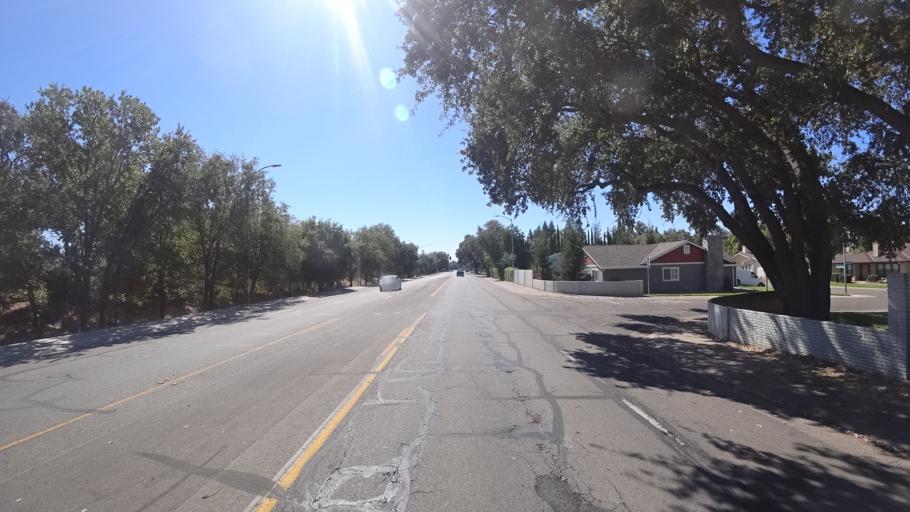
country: US
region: California
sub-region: Sacramento County
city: Elk Grove
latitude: 38.4030
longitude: -121.3715
